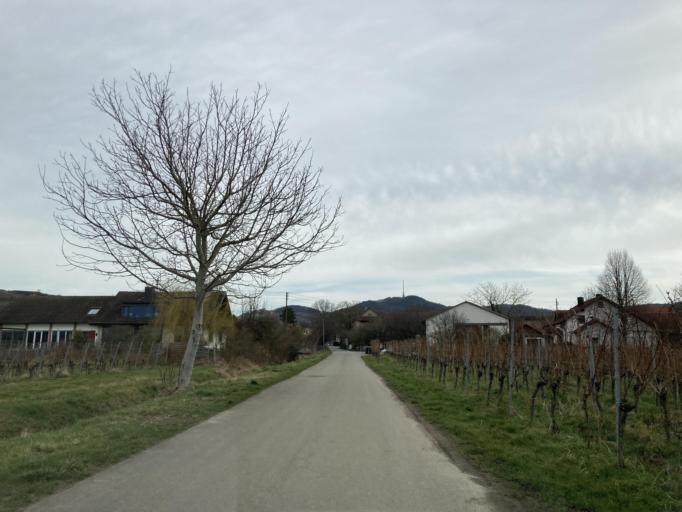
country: DE
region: Baden-Wuerttemberg
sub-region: Freiburg Region
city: Vogtsburg
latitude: 48.0907
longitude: 7.6186
